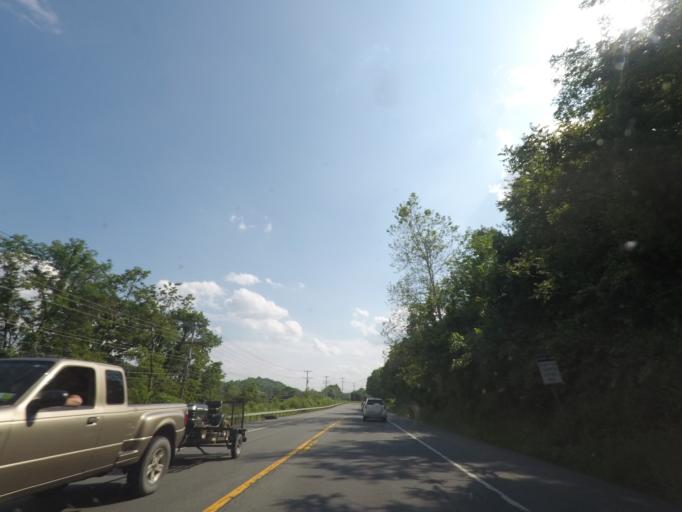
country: US
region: New York
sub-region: Ulster County
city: Marlboro
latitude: 41.5860
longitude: -73.9835
